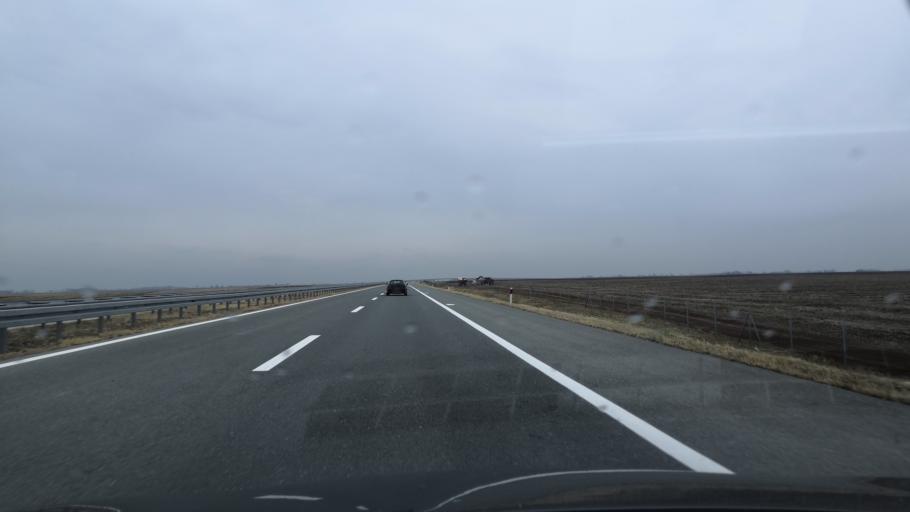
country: RS
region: Autonomna Pokrajina Vojvodina
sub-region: Severnobacki Okrug
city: Mali Igos
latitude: 45.7155
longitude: 19.7124
